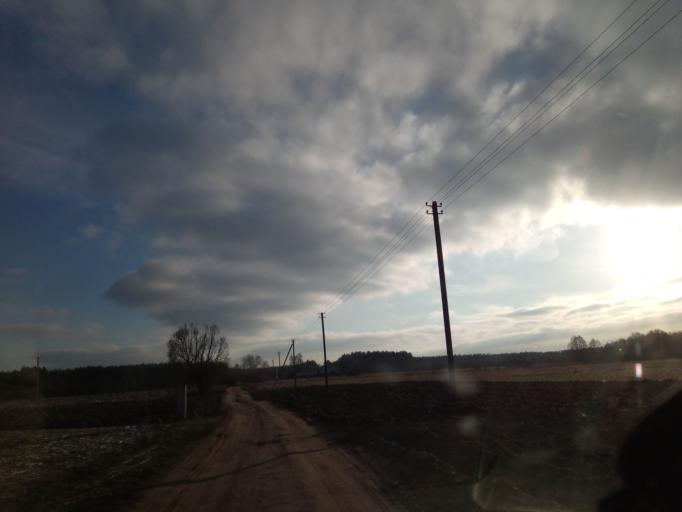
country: LT
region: Alytaus apskritis
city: Druskininkai
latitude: 53.9801
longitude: 24.2415
